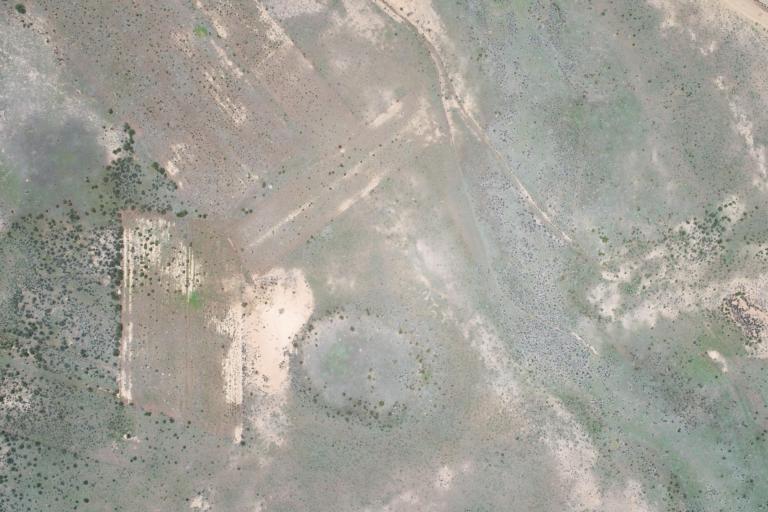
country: BO
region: La Paz
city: Curahuara de Carangas
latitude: -17.2851
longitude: -68.5126
